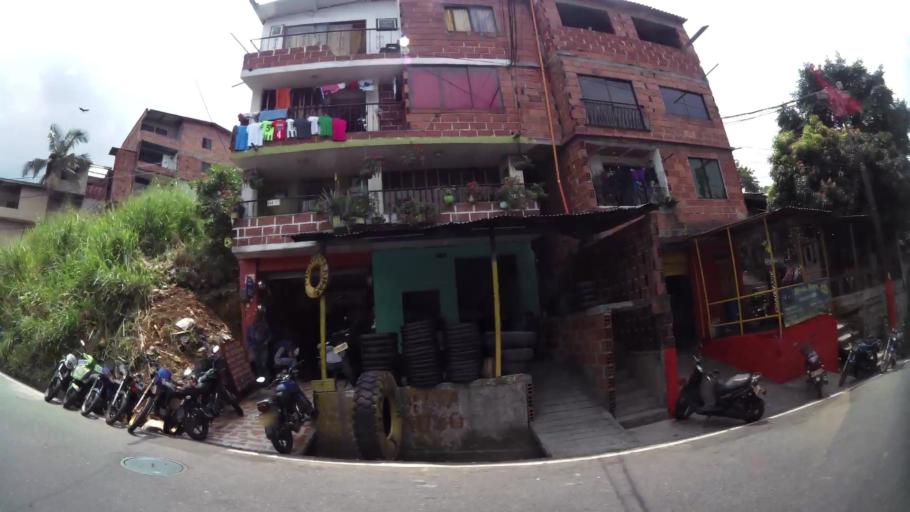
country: CO
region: Antioquia
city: Medellin
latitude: 6.2626
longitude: -75.5544
